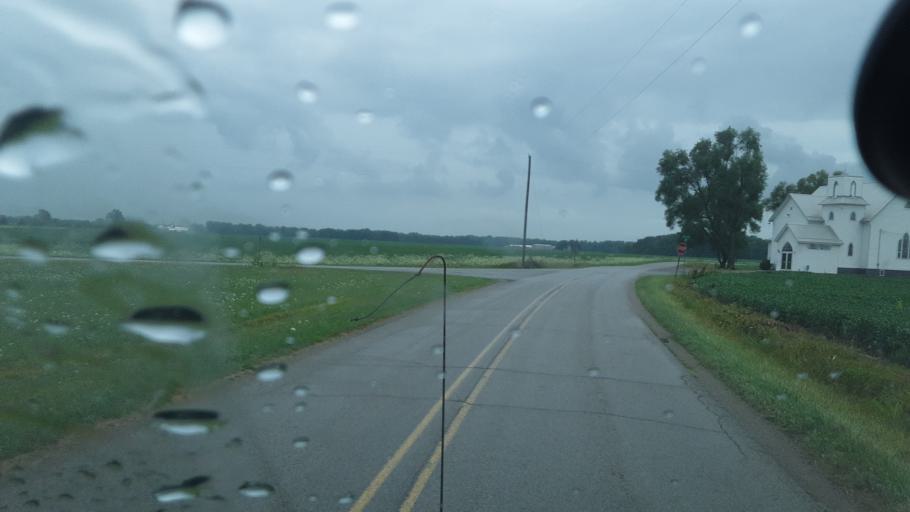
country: US
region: Ohio
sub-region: Williams County
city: Edgerton
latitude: 41.5035
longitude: -84.8142
